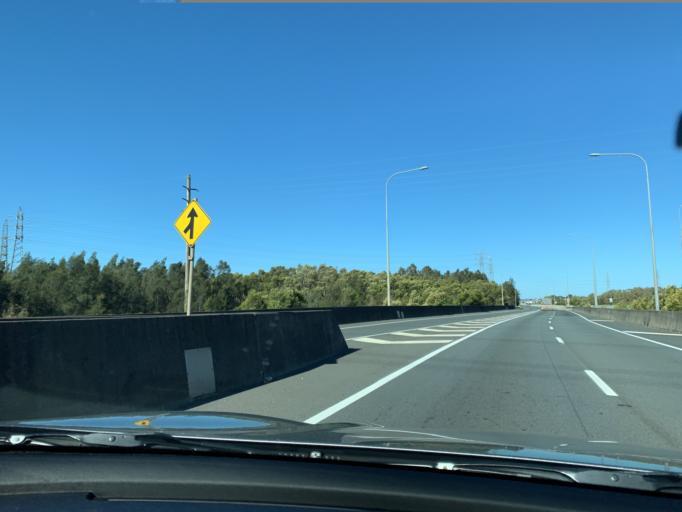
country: AU
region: Queensland
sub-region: Brisbane
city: Cannon Hill
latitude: -27.4510
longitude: 153.1157
